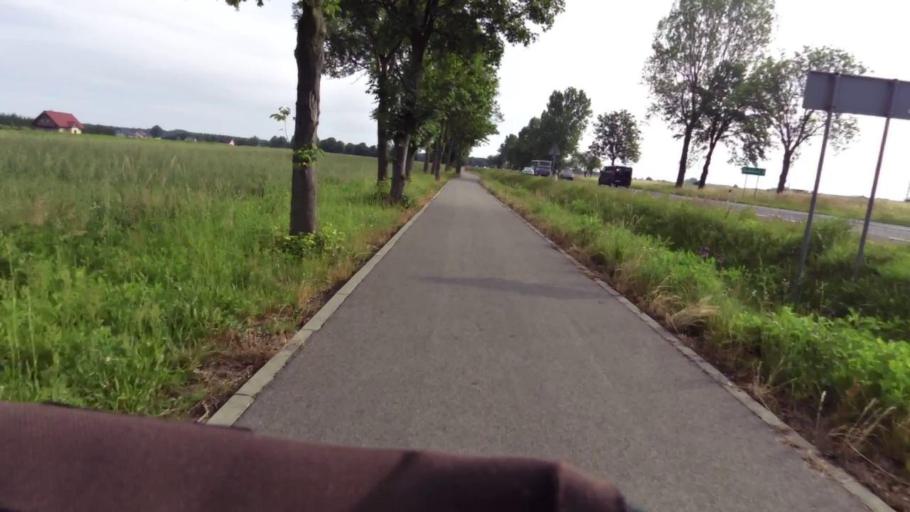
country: PL
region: West Pomeranian Voivodeship
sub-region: Powiat kamienski
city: Kamien Pomorski
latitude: 53.9825
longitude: 14.7969
